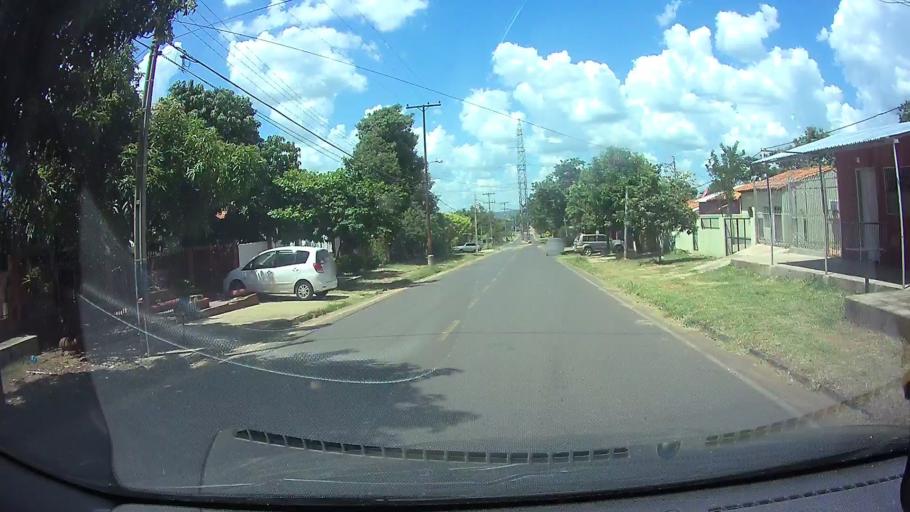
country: PY
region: Central
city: Limpio
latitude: -25.1676
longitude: -57.4381
